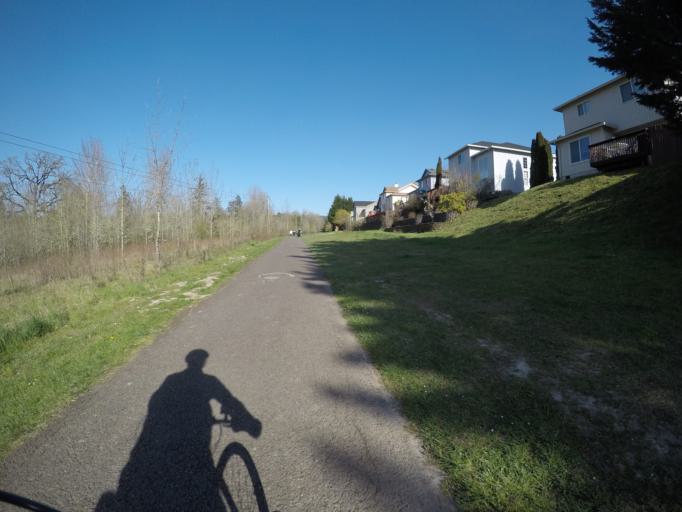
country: US
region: Oregon
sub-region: Washington County
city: Oak Hills
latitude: 45.5613
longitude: -122.8408
